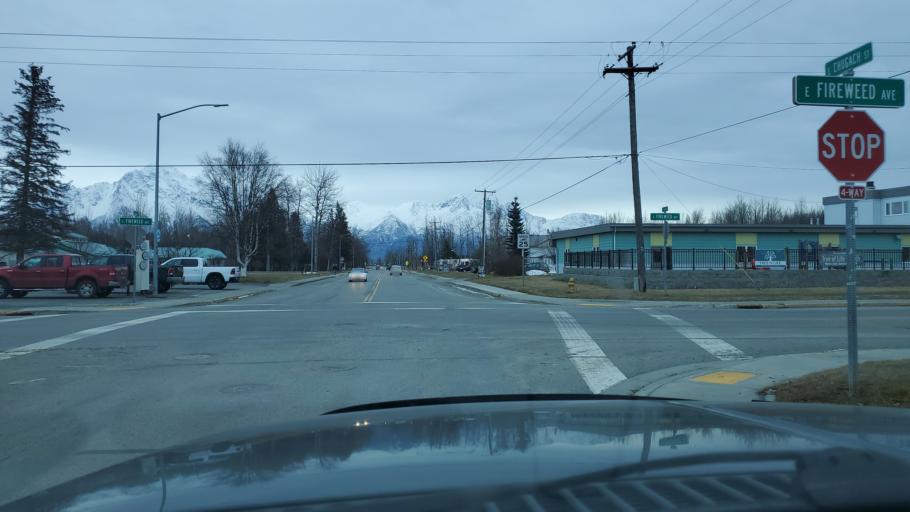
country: US
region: Alaska
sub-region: Matanuska-Susitna Borough
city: Palmer
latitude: 61.5980
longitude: -149.1108
